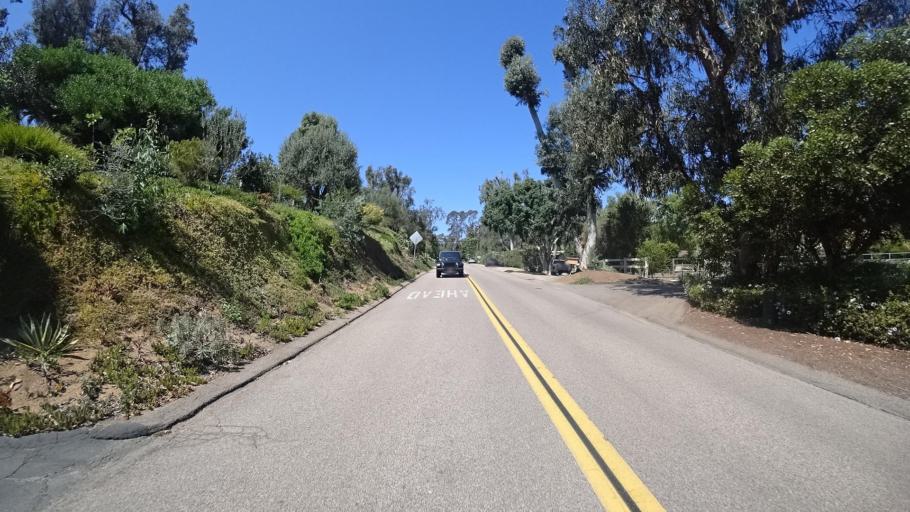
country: US
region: California
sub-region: San Diego County
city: Rancho Santa Fe
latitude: 32.9913
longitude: -117.2292
